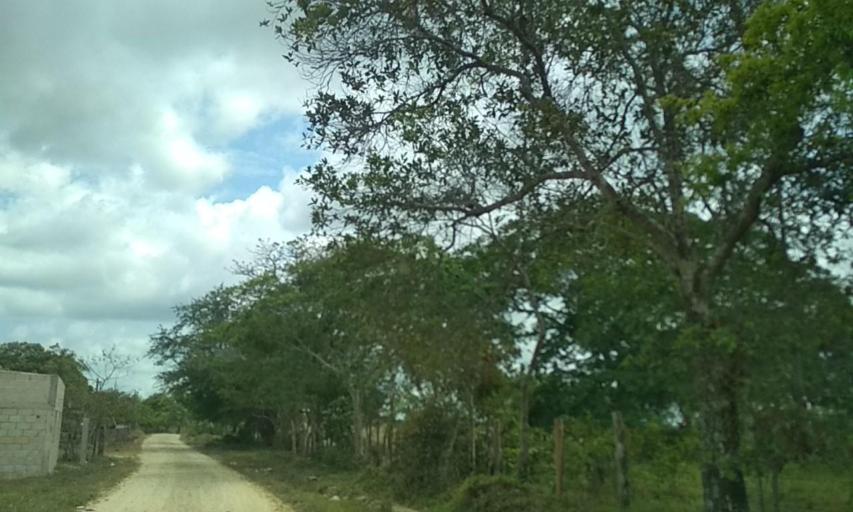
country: MX
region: Veracruz
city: Las Choapas
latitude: 17.8970
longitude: -94.1188
